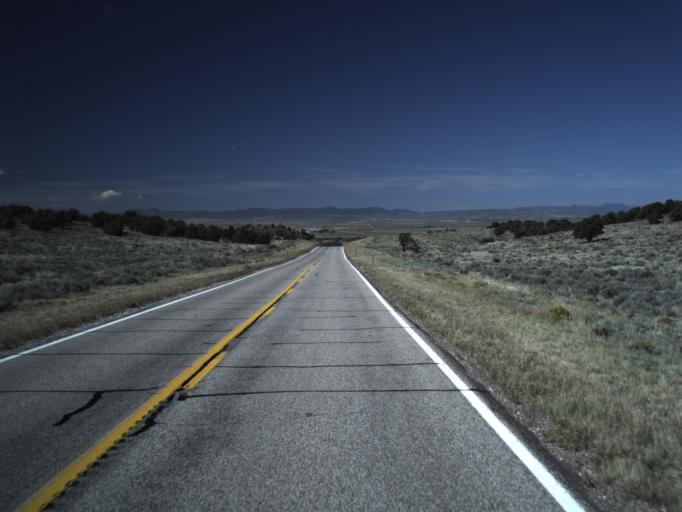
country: US
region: Utah
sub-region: Washington County
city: Enterprise
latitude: 37.6758
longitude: -113.5013
